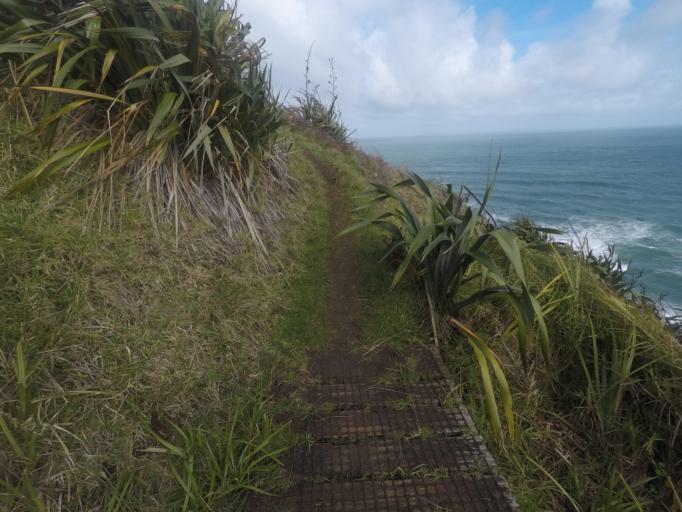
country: NZ
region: Auckland
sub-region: Auckland
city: Muriwai Beach
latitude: -36.8618
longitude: 174.4335
